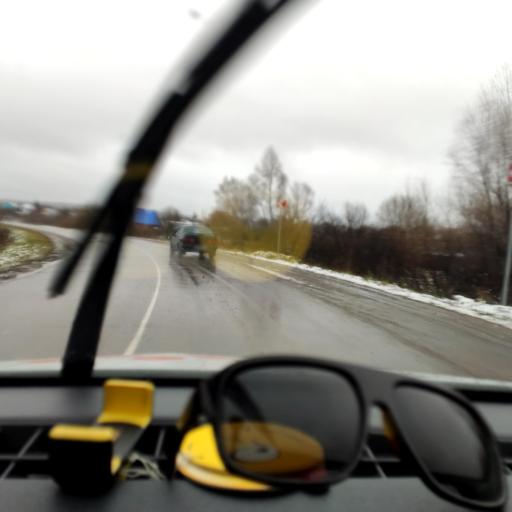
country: RU
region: Bashkortostan
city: Iglino
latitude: 54.8760
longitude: 56.5556
